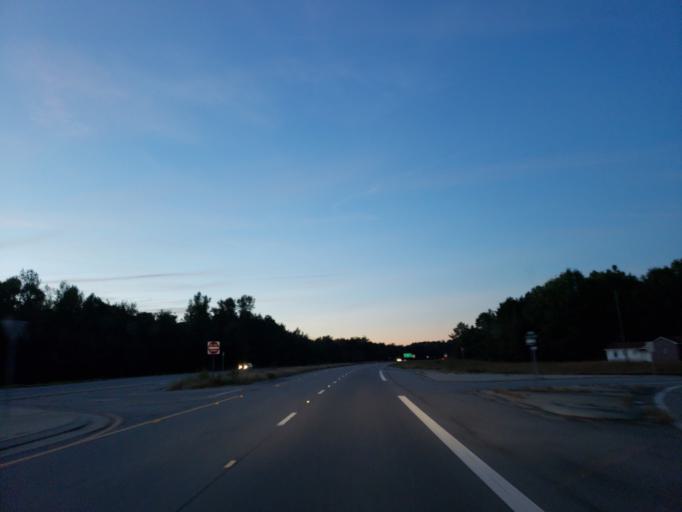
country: US
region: Mississippi
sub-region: Wayne County
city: Waynesboro
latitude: 31.8502
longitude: -88.7172
